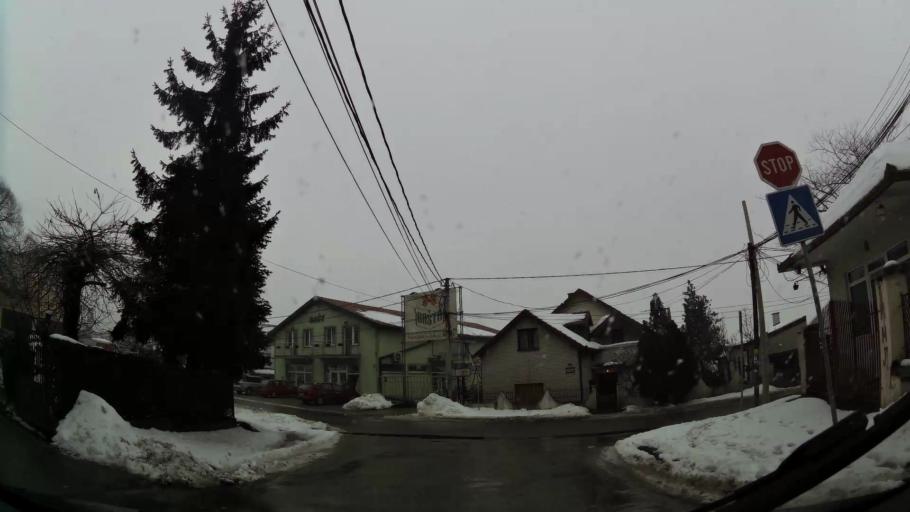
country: RS
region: Central Serbia
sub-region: Belgrade
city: Zvezdara
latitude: 44.7773
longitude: 20.5294
